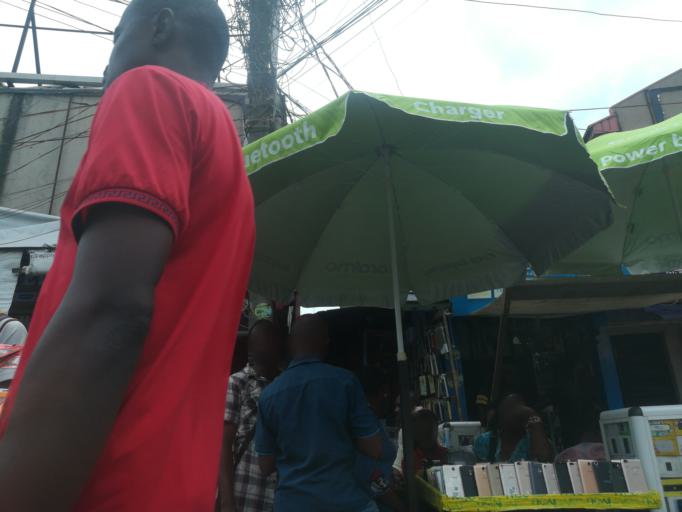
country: NG
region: Lagos
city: Ikeja
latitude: 6.5959
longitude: 3.3402
